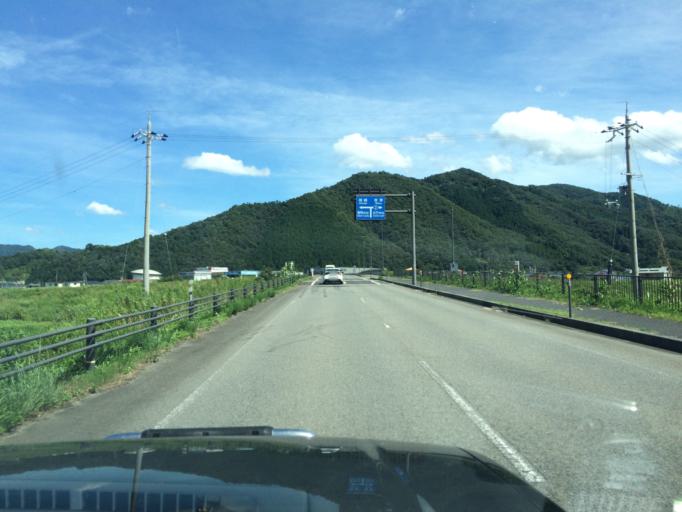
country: JP
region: Hyogo
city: Toyooka
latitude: 35.4682
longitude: 134.8639
